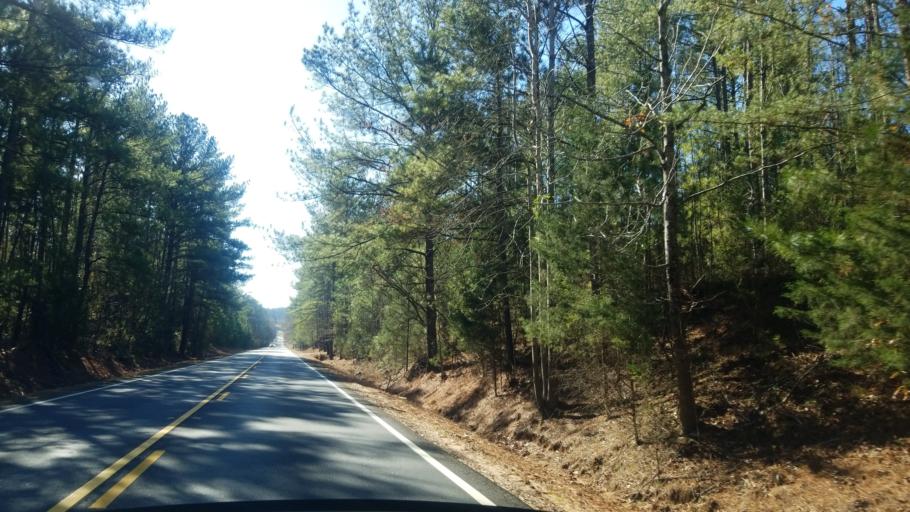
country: US
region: Alabama
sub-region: Chambers County
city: Valley
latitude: 32.8025
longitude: -85.1029
